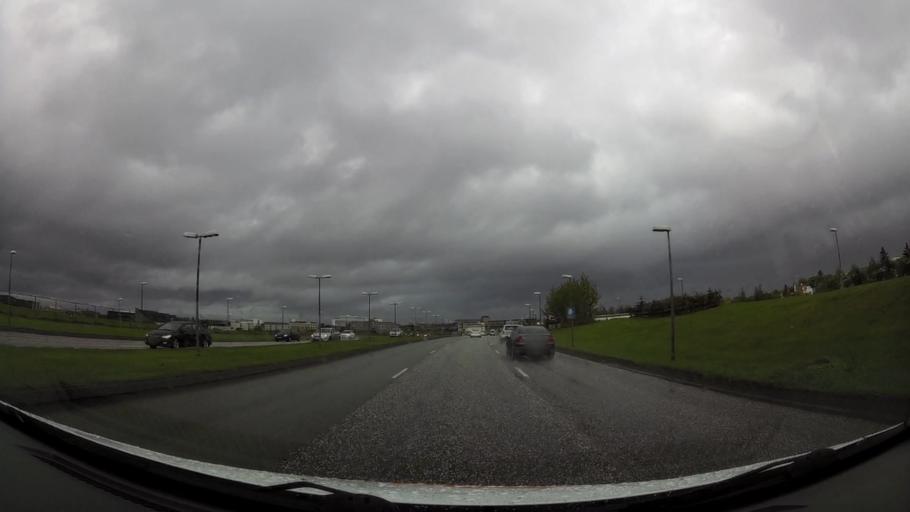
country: IS
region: Capital Region
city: Kopavogur
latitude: 64.1374
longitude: -21.9367
